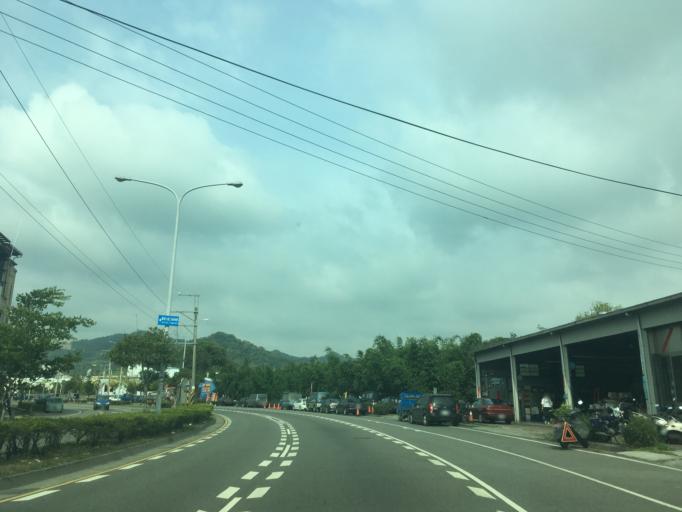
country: TW
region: Taiwan
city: Fengyuan
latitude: 24.2361
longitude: 120.7246
